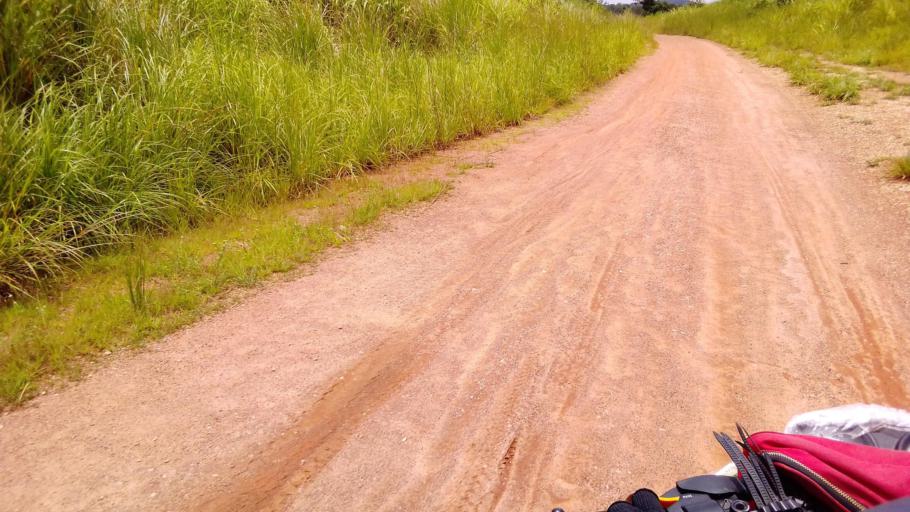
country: SL
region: Eastern Province
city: Koidu
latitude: 8.6724
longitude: -10.9552
